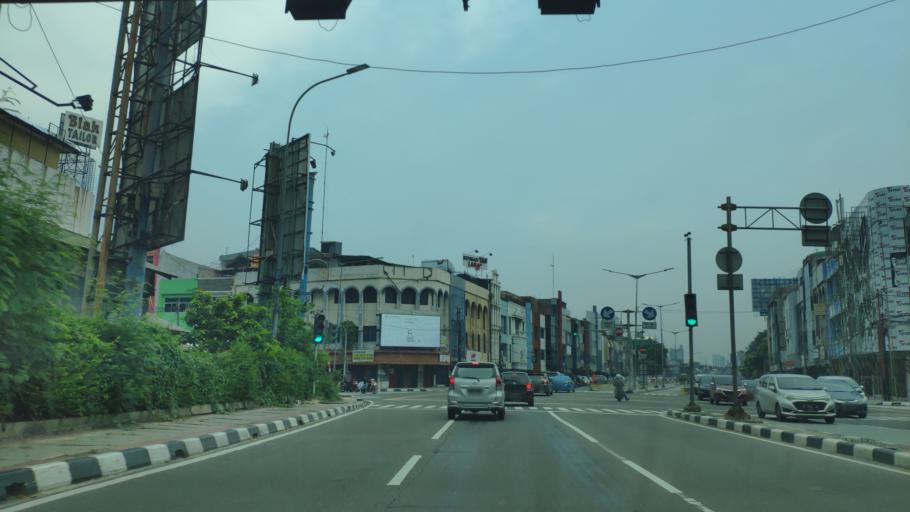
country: ID
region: Jakarta Raya
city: Jakarta
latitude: -6.1716
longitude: 106.8083
